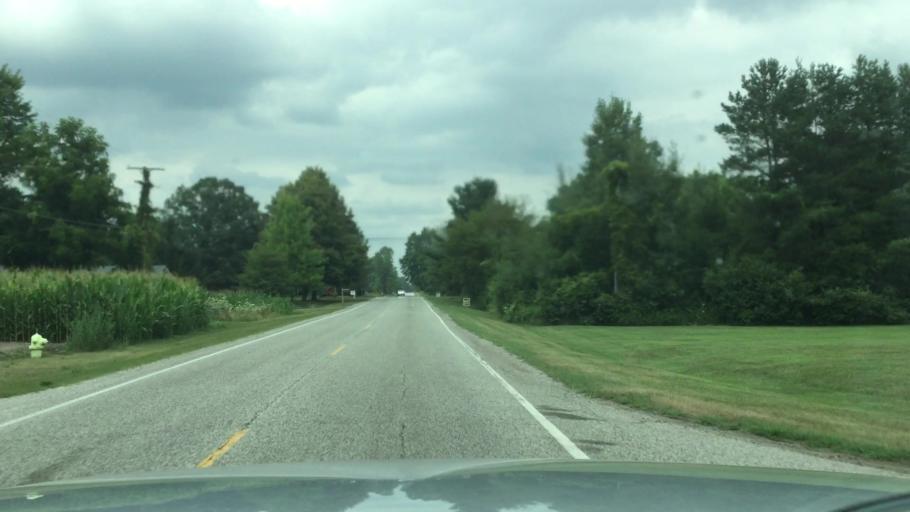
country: US
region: Michigan
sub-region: Saginaw County
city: Bridgeport
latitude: 43.3099
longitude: -83.8945
